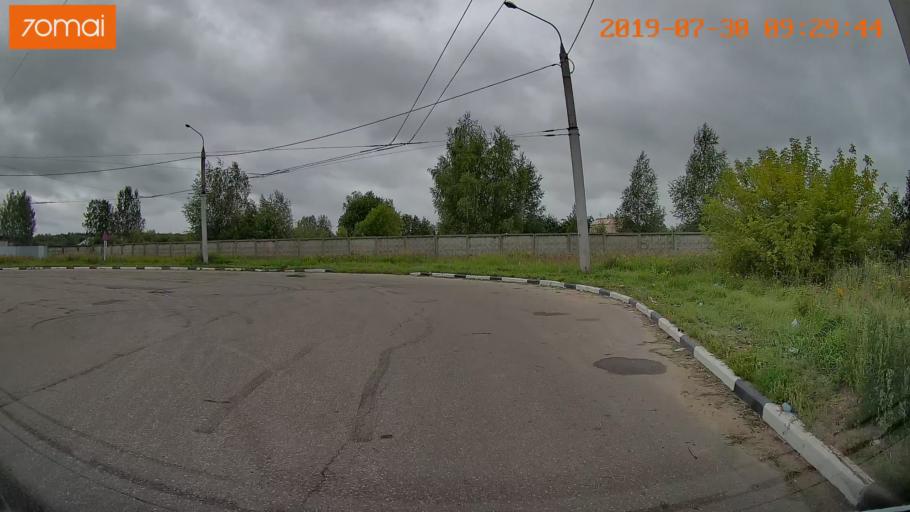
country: RU
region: Ivanovo
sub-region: Gorod Ivanovo
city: Ivanovo
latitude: 56.9435
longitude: 40.9435
